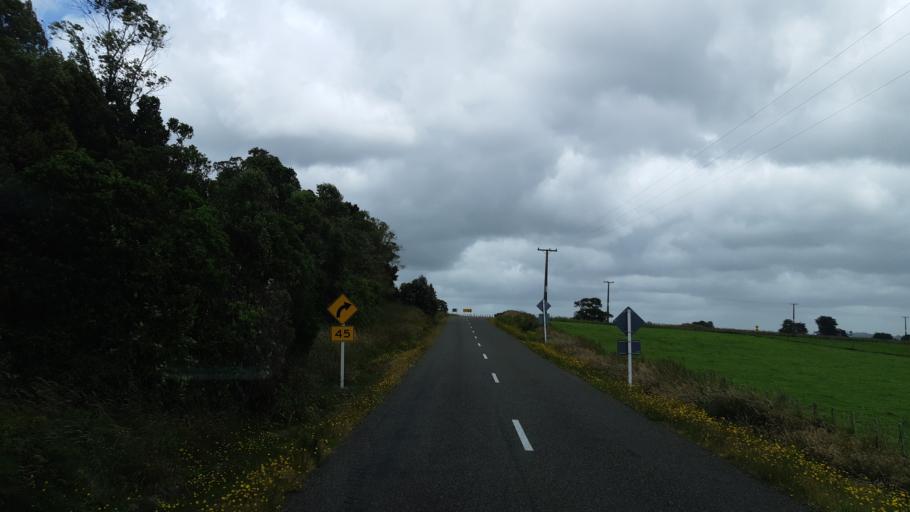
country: NZ
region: Manawatu-Wanganui
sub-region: Palmerston North City
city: Palmerston North
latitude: -39.9378
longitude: 175.9137
